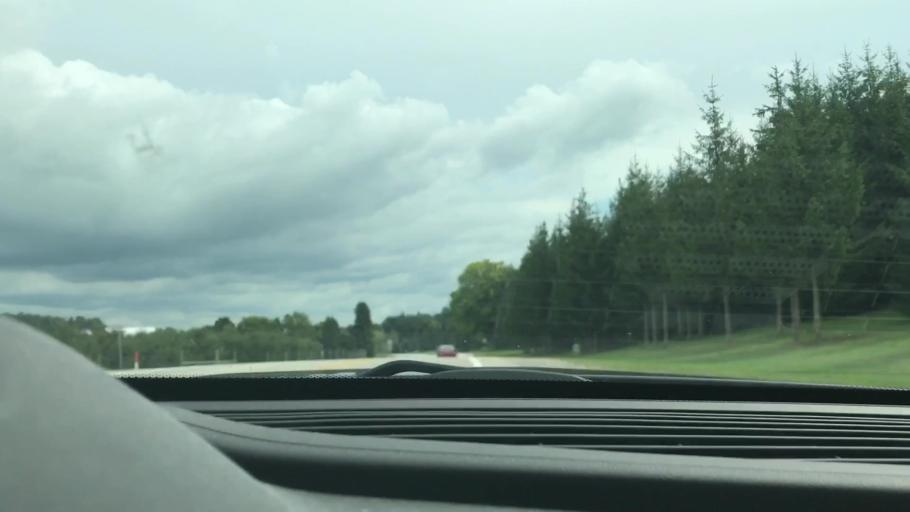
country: US
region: Michigan
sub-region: Antrim County
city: Bellaire
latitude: 45.0985
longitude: -85.3019
